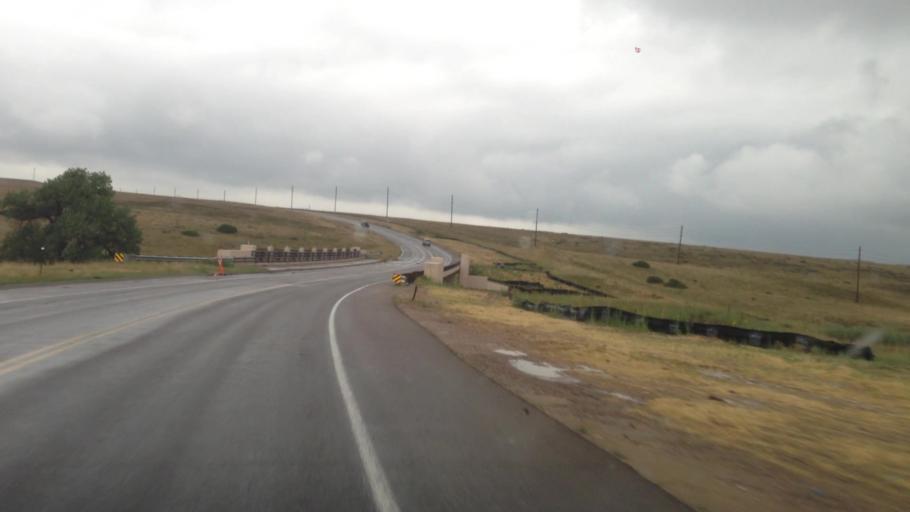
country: US
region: Colorado
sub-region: Douglas County
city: Stonegate
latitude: 39.5199
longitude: -104.8336
